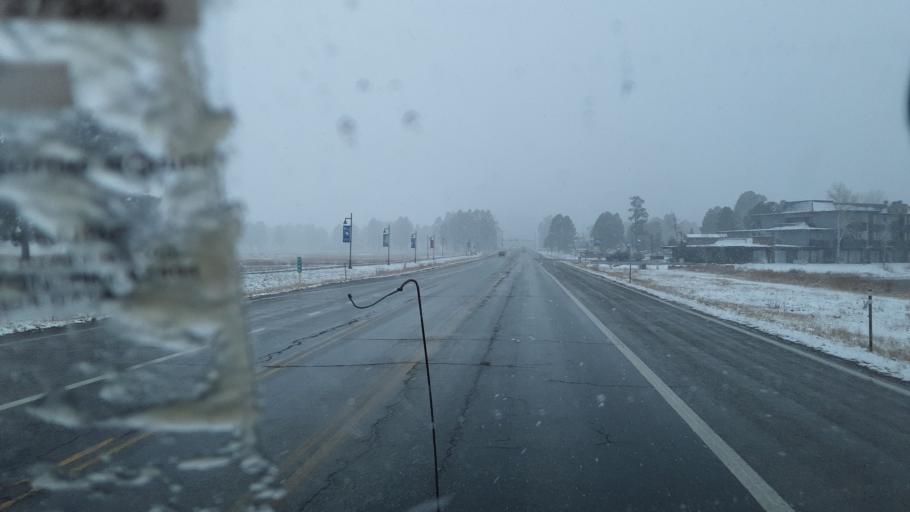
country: US
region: Colorado
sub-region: Archuleta County
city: Pagosa Springs
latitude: 37.2611
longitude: -107.0652
